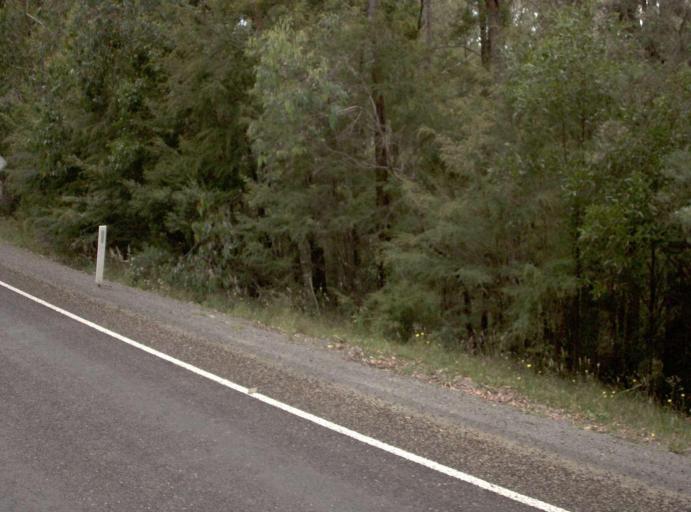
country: AU
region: Victoria
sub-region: Latrobe
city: Traralgon
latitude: -38.1148
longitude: 146.4515
